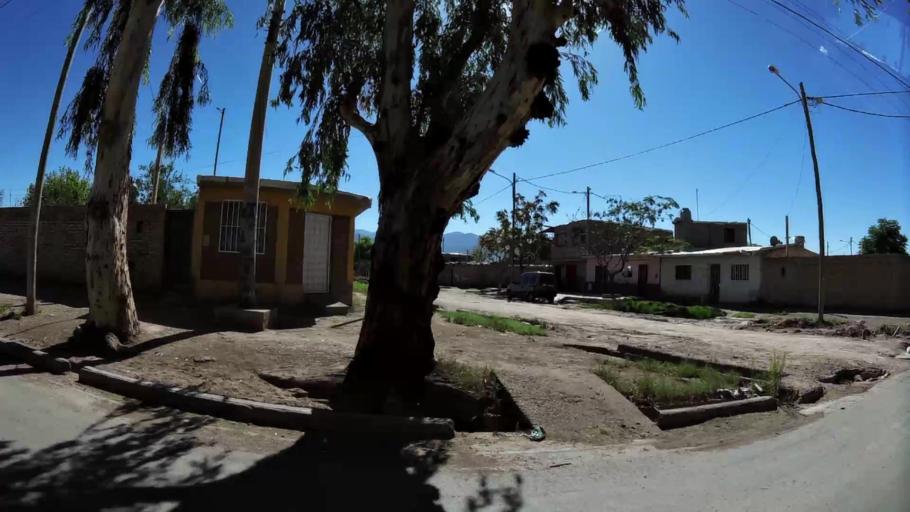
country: AR
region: Mendoza
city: Las Heras
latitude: -32.8311
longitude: -68.8168
